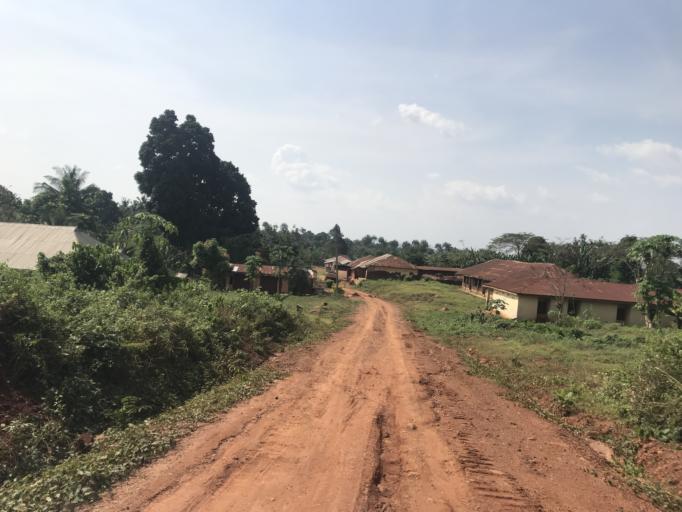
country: NG
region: Osun
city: Ilesa
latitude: 7.6353
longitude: 4.6731
